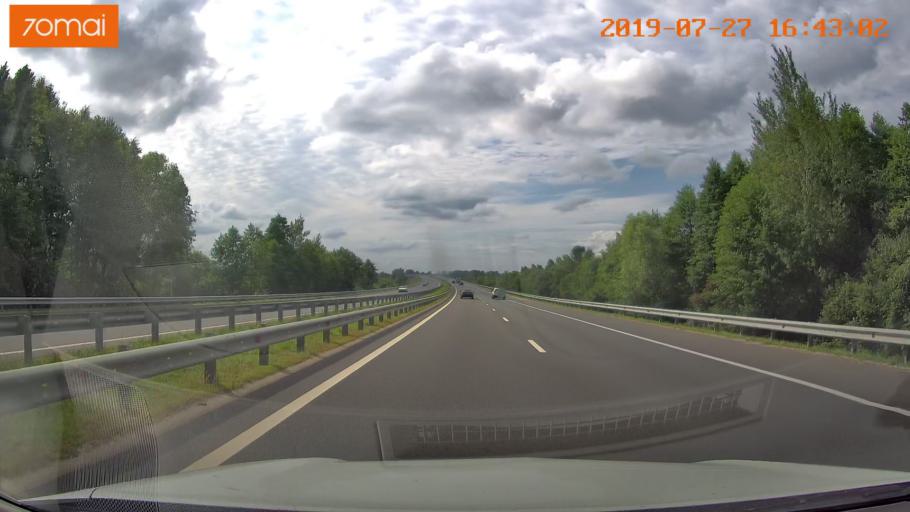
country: RU
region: Kaliningrad
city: Gvardeysk
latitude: 54.6689
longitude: 21.1127
